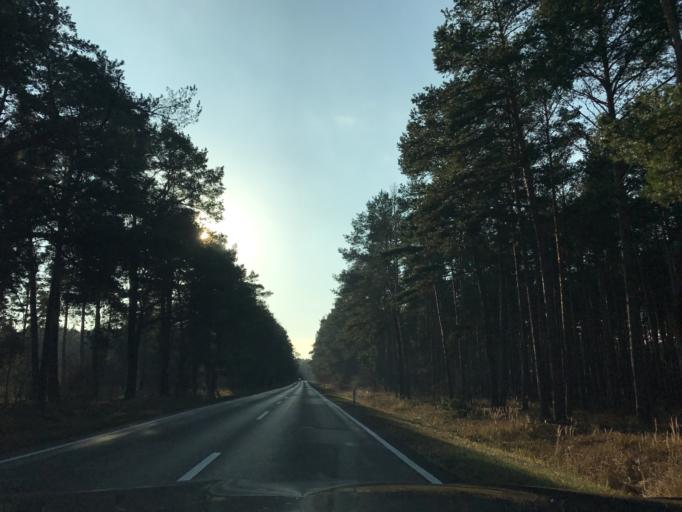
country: DE
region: Brandenburg
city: Wenzlow
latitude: 52.3140
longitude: 12.4784
